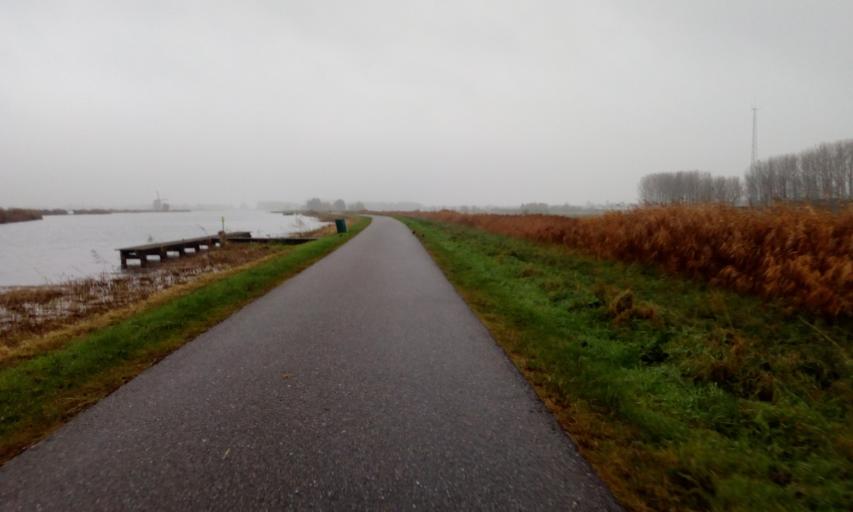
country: NL
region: South Holland
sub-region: Gemeente Lansingerland
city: Bleiswijk
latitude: 52.0296
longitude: 4.5582
